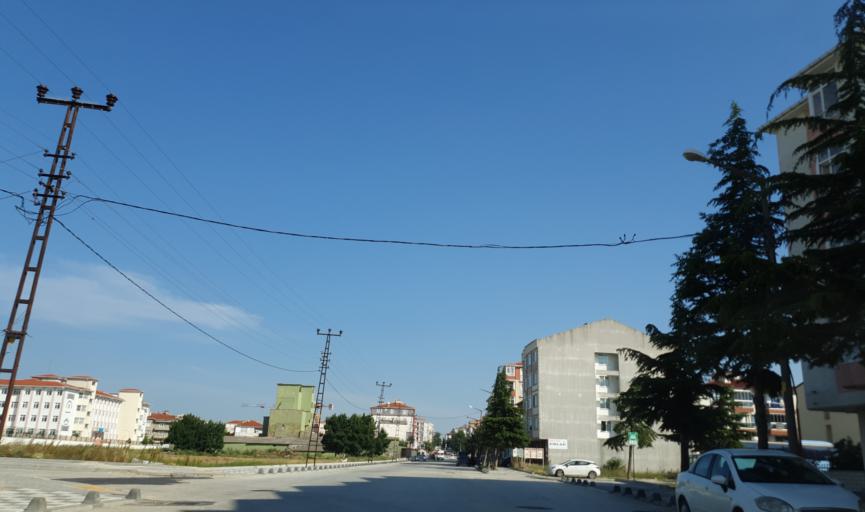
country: TR
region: Tekirdag
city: Saray
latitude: 41.4473
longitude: 27.9151
